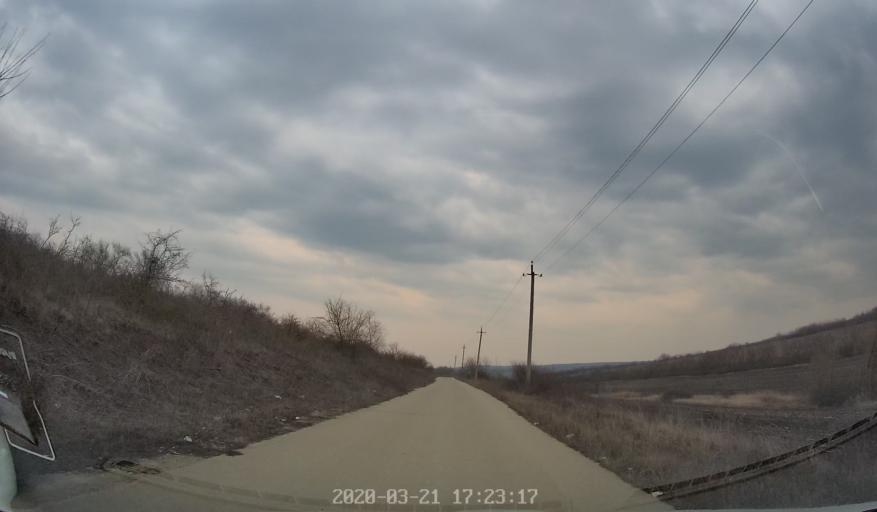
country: MD
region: Laloveni
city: Ialoveni
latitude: 46.9321
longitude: 28.6984
